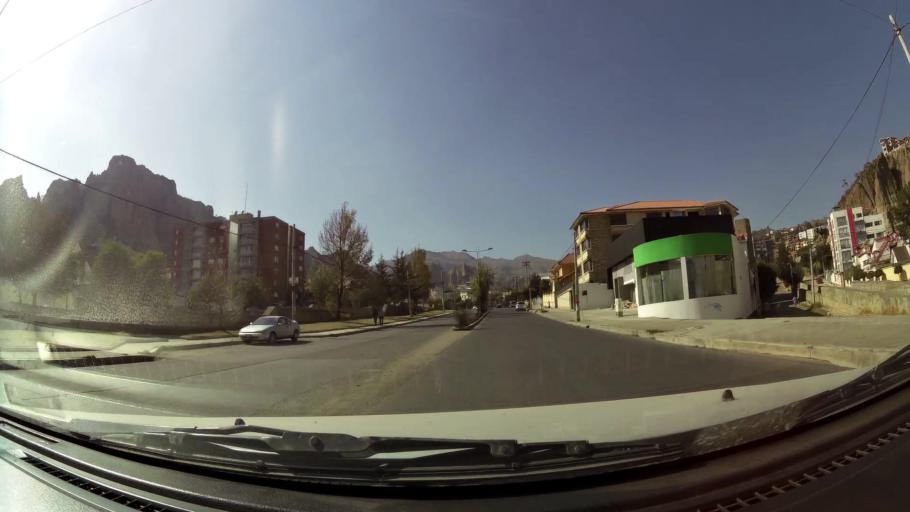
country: BO
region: La Paz
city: La Paz
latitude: -16.5246
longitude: -68.0674
